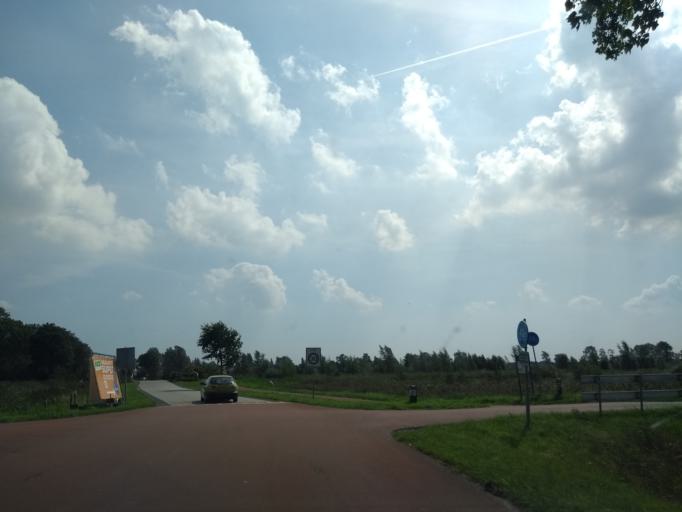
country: NL
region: Friesland
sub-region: Sudwest Fryslan
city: Oppenhuizen
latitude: 53.0343
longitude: 5.7188
